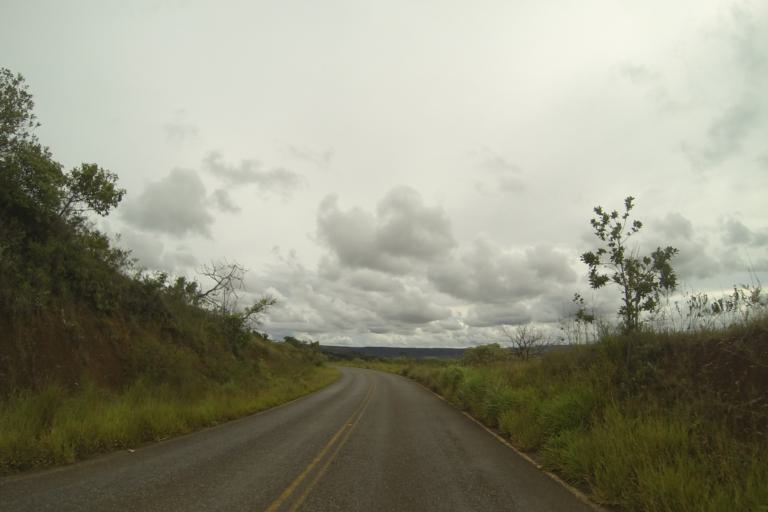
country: BR
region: Minas Gerais
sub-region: Ibia
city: Ibia
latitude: -19.6851
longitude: -46.4444
